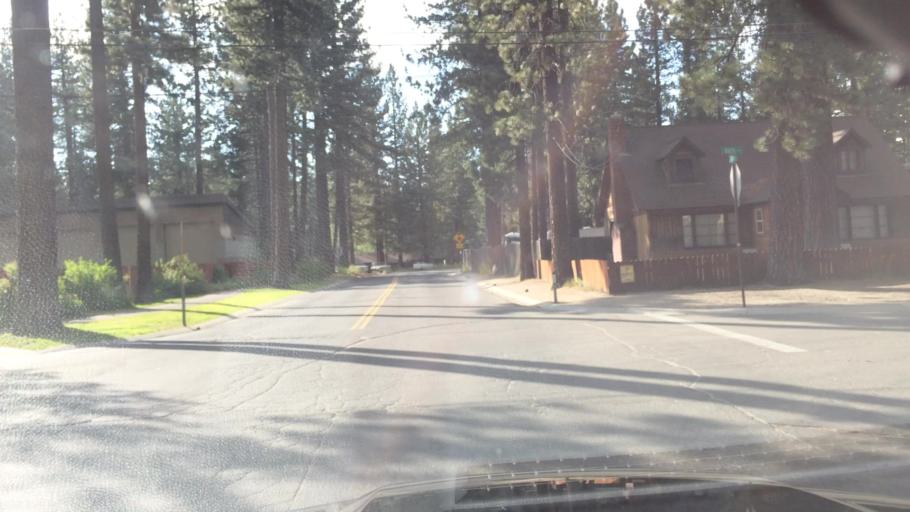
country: US
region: California
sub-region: El Dorado County
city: South Lake Tahoe
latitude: 38.9189
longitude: -120.0012
